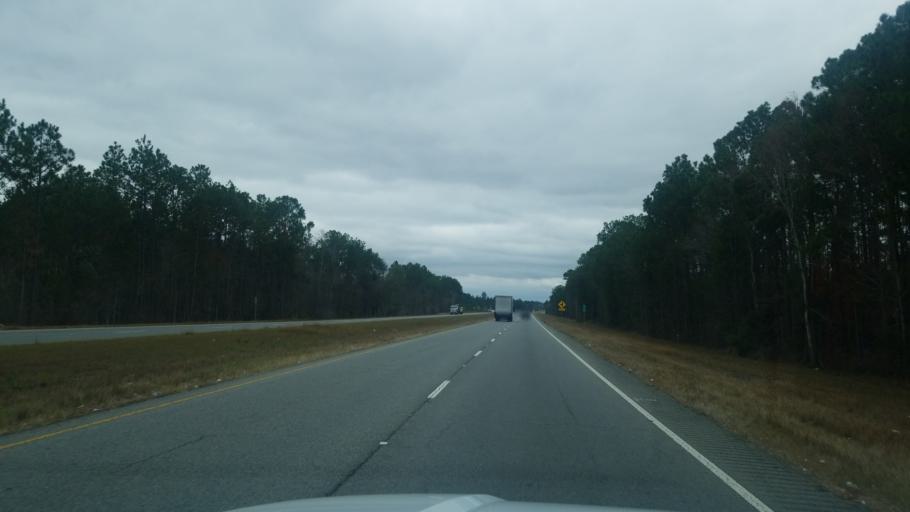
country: US
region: Georgia
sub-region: Ware County
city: Deenwood
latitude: 31.2201
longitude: -82.4232
